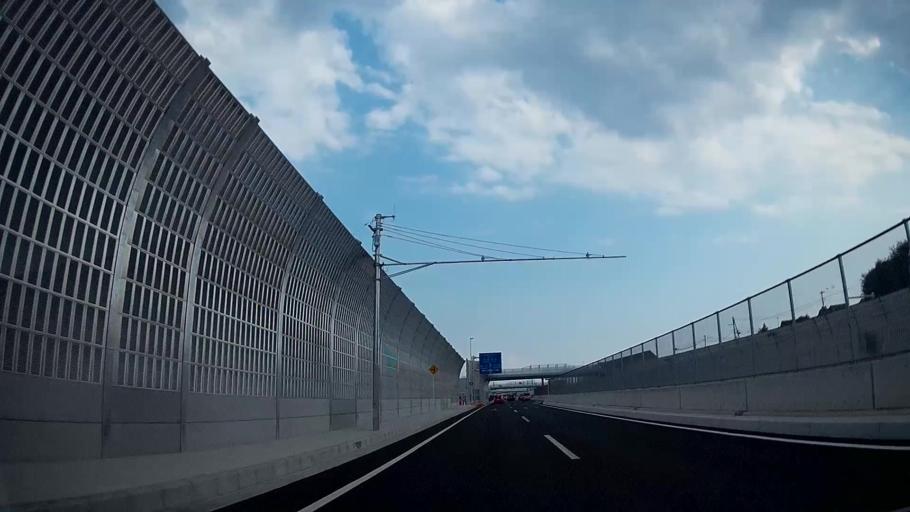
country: JP
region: Chiba
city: Matsudo
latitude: 35.7458
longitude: 139.9197
